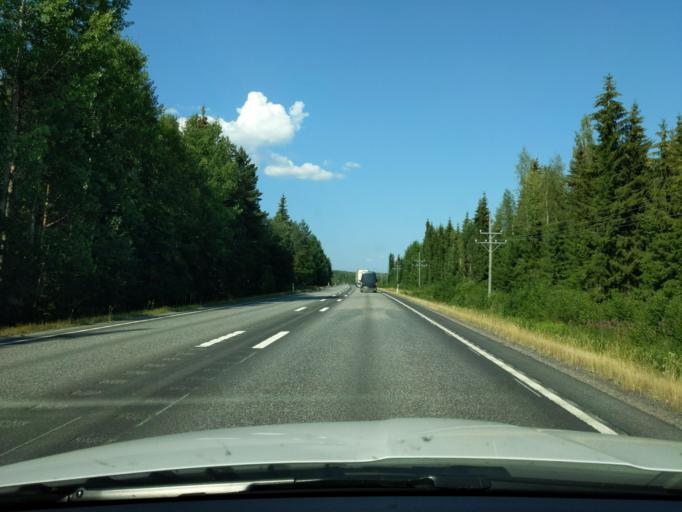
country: FI
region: Paijanne Tavastia
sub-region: Lahti
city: Jaervelae
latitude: 60.9173
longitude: 25.3555
